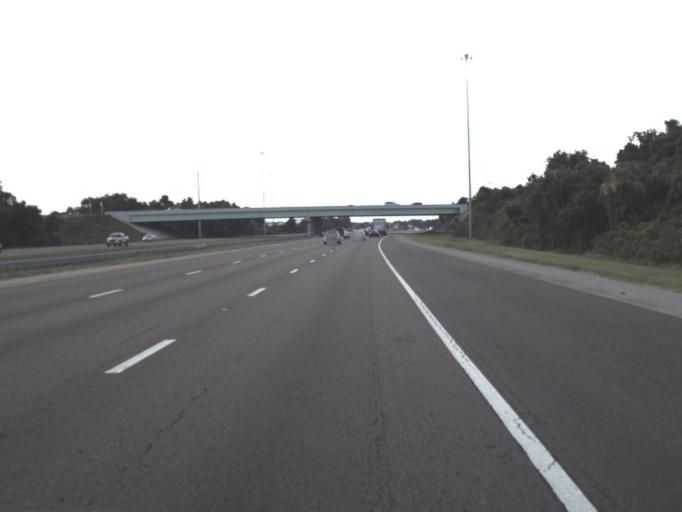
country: US
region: Florida
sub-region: Hillsborough County
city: Riverview
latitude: 27.8544
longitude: -82.3468
